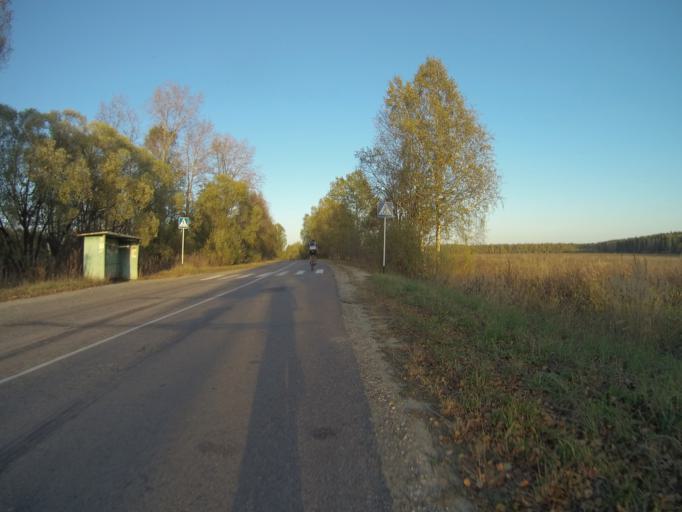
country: RU
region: Vladimir
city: Golovino
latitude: 55.9611
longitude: 40.5069
